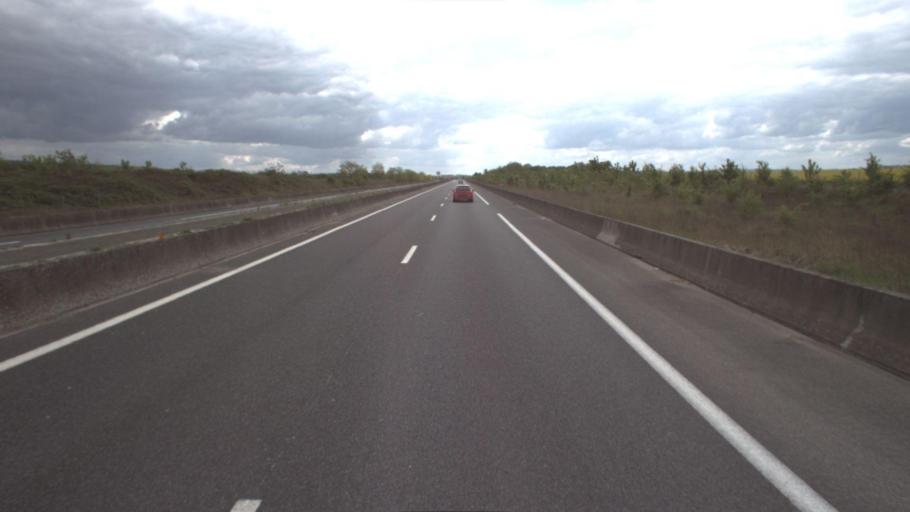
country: FR
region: Ile-de-France
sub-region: Departement de Seine-et-Marne
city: Mareuil-les-Meaux
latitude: 48.9322
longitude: 2.8459
